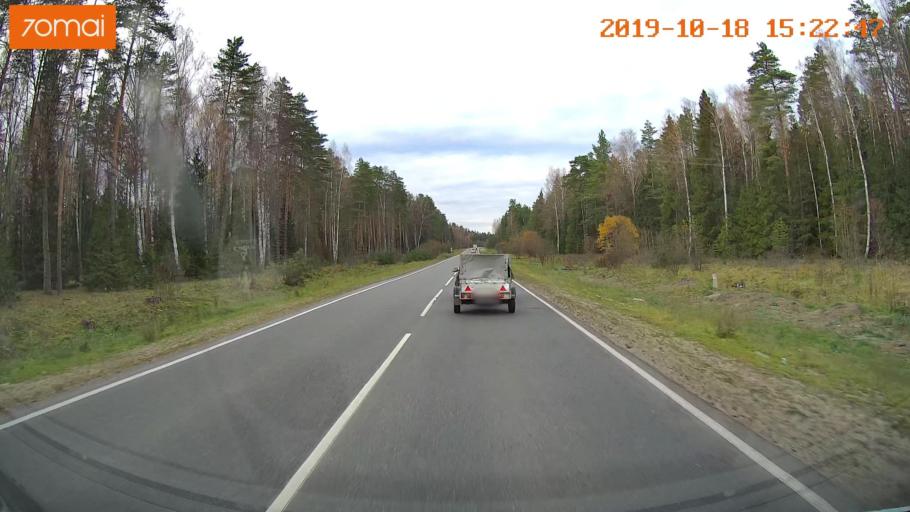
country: RU
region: Vladimir
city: Anopino
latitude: 55.7114
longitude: 40.7283
